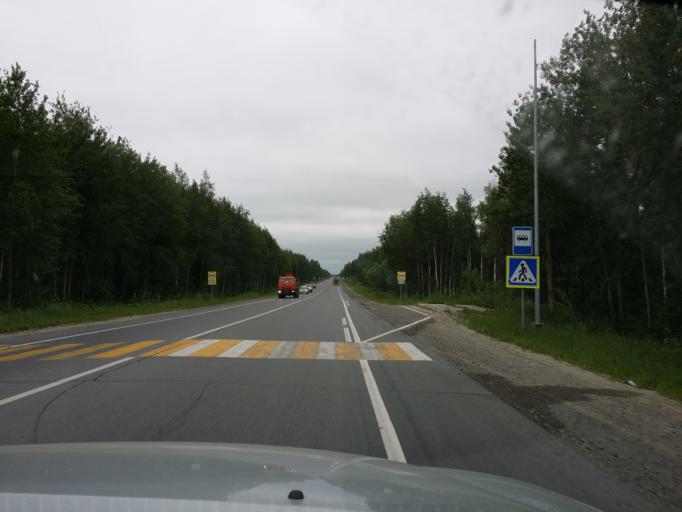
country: RU
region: Khanty-Mansiyskiy Avtonomnyy Okrug
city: Megion
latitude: 61.0594
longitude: 76.2883
